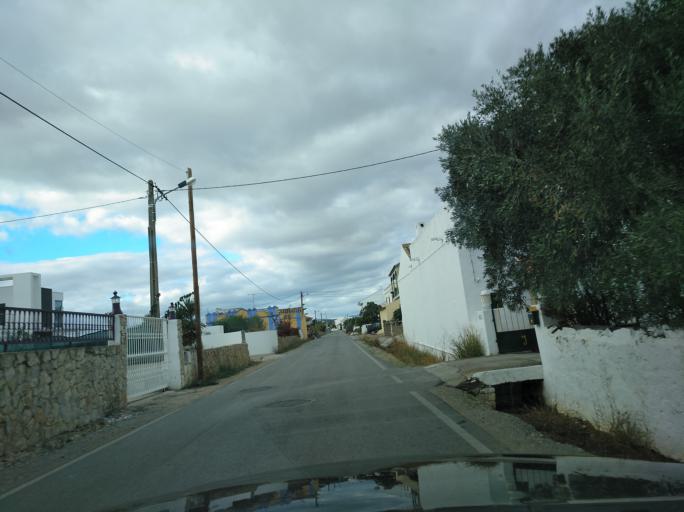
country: PT
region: Faro
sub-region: Tavira
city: Luz
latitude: 37.0987
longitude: -7.7069
